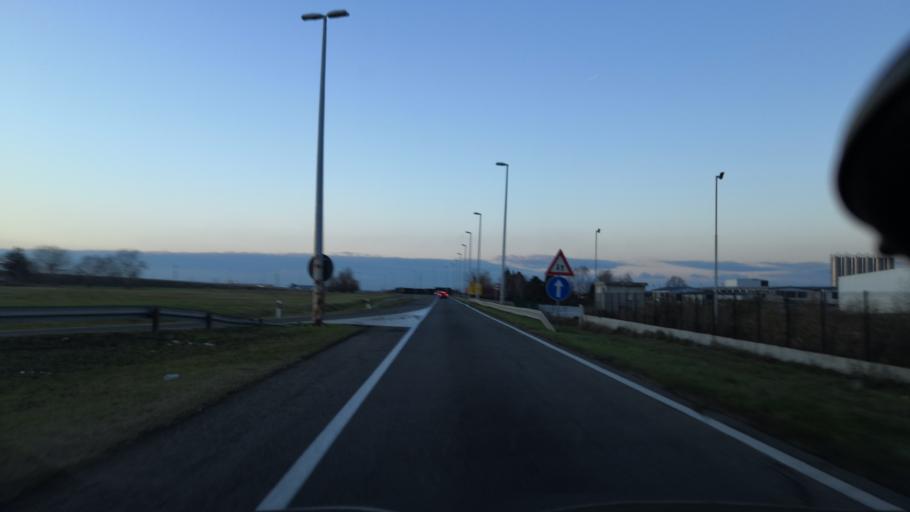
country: RS
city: Simanovci
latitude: 44.8749
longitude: 20.1310
